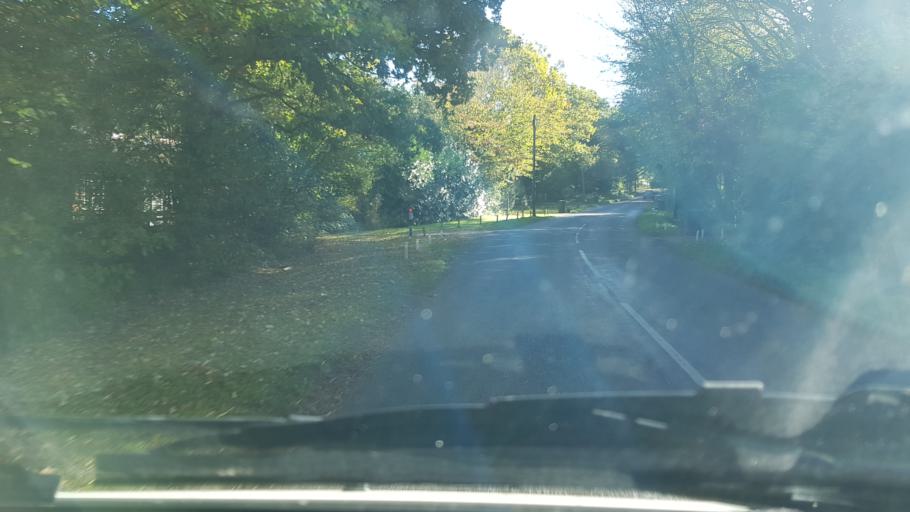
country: GB
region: England
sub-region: West Sussex
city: Rudgwick
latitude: 51.1350
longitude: -0.4236
